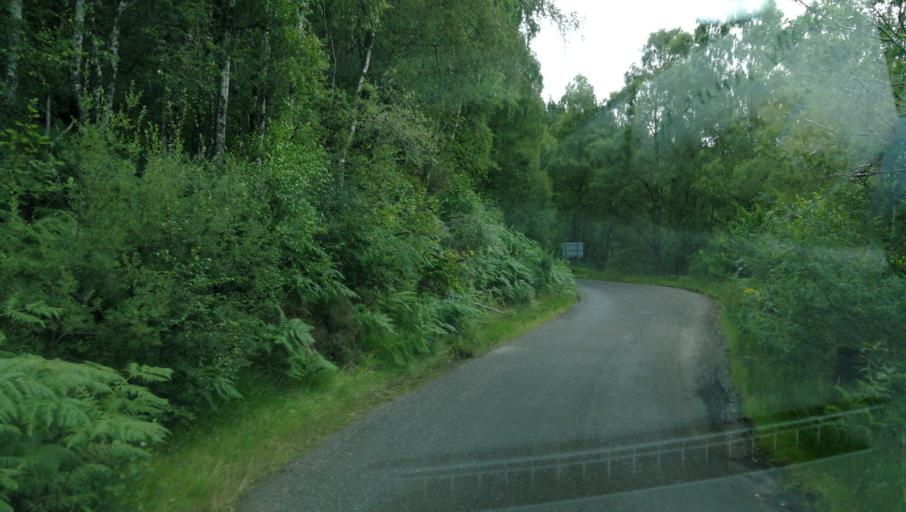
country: GB
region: Scotland
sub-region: Highland
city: Beauly
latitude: 57.3177
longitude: -4.8278
